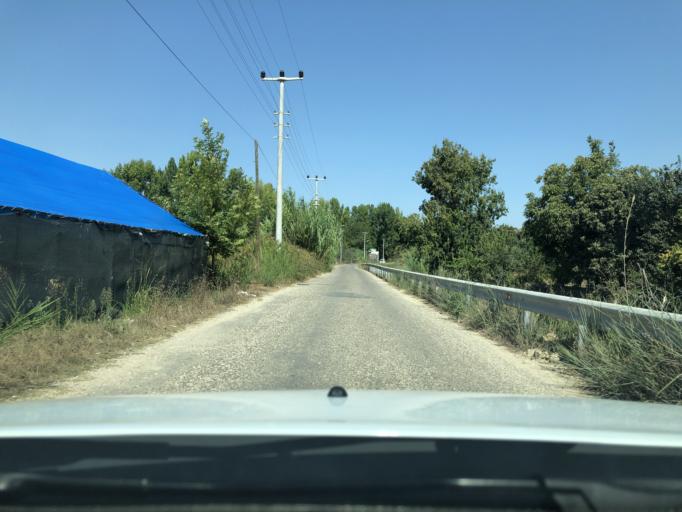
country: TR
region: Antalya
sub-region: Manavgat
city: Manavgat
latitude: 36.8060
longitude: 31.4655
